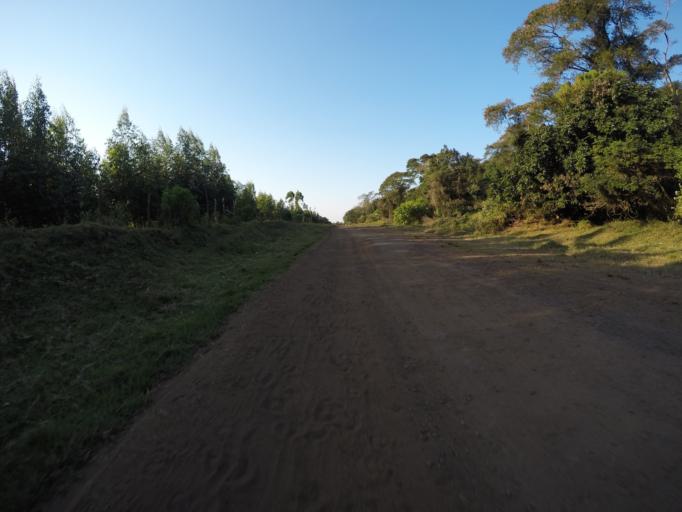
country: ZA
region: KwaZulu-Natal
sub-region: uThungulu District Municipality
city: KwaMbonambi
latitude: -28.6965
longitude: 32.1959
